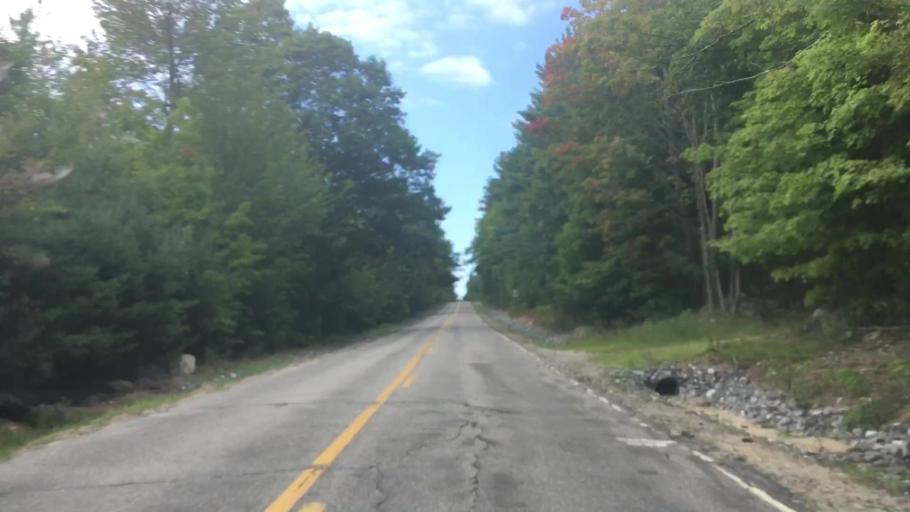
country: US
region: Maine
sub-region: Oxford County
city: Oxford
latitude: 44.0714
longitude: -70.5441
